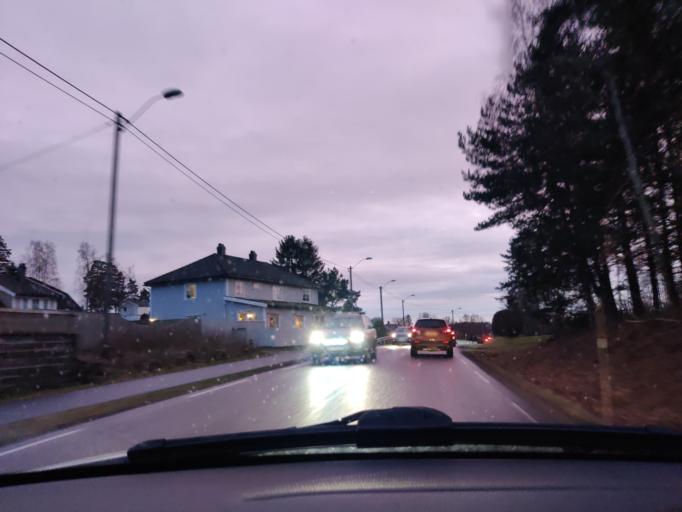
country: NO
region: Vestfold
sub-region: Tonsberg
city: Sem
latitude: 59.2627
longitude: 10.3631
